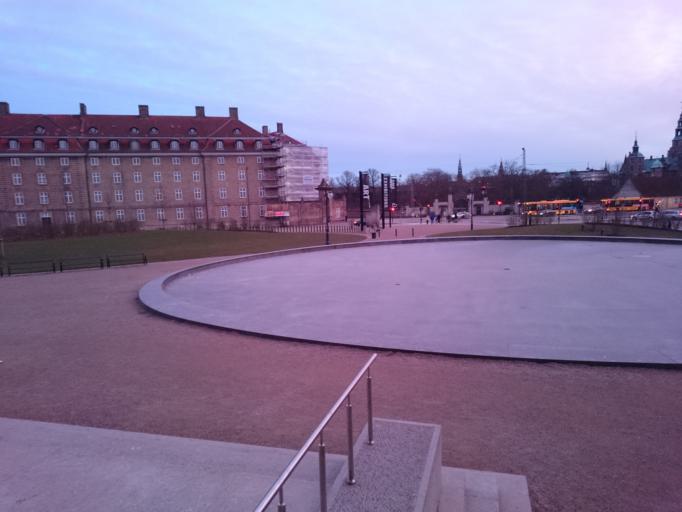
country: DK
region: Capital Region
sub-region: Kobenhavn
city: Copenhagen
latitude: 55.6883
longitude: 12.5781
